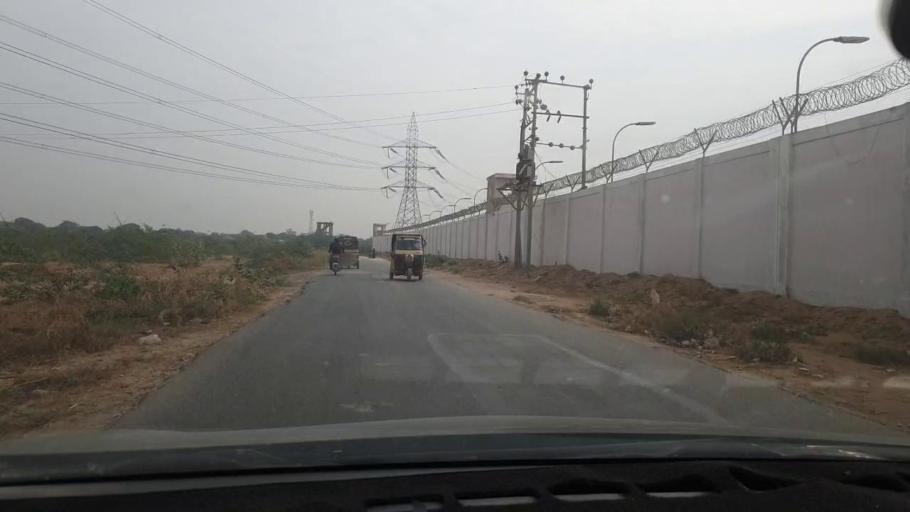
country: PK
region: Sindh
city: Malir Cantonment
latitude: 24.9112
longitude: 67.2834
